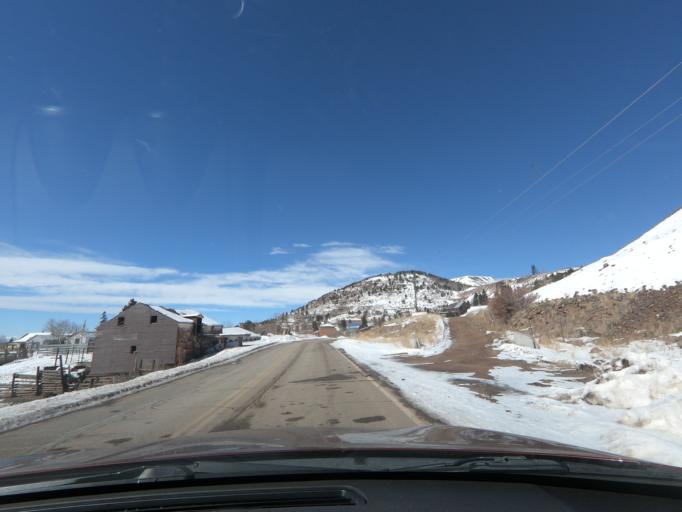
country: US
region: Colorado
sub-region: Teller County
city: Cripple Creek
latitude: 38.7105
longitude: -105.1353
